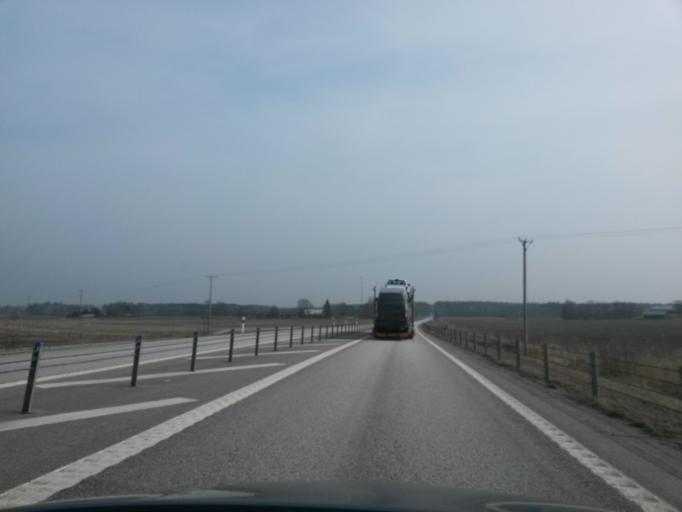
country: SE
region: Vaestra Goetaland
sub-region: Gullspangs Kommun
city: Hova
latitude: 58.8231
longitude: 14.1527
